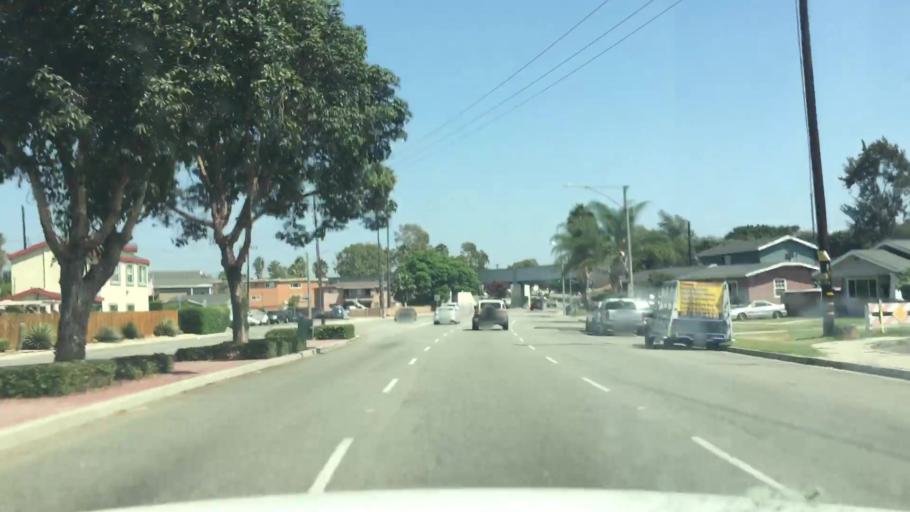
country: US
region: California
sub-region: Los Angeles County
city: Signal Hill
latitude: 33.8463
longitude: -118.1892
